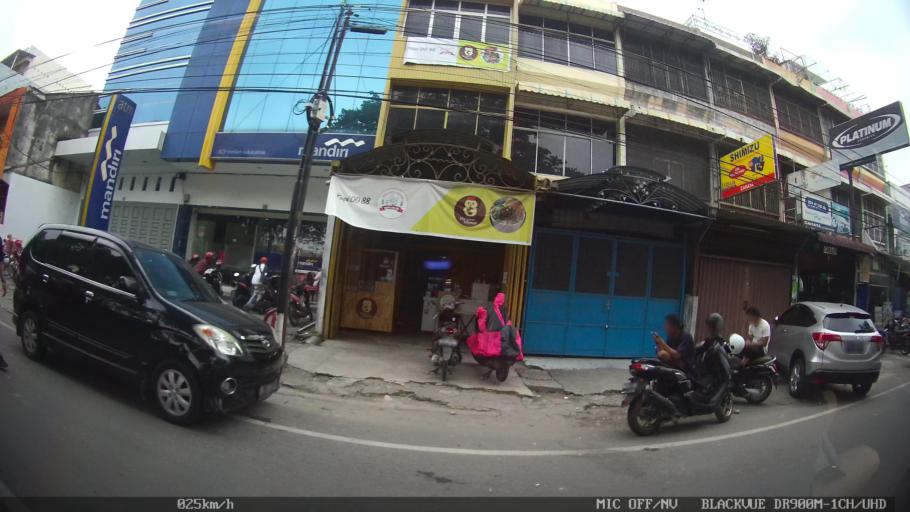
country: ID
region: North Sumatra
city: Medan
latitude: 3.5772
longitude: 98.7035
